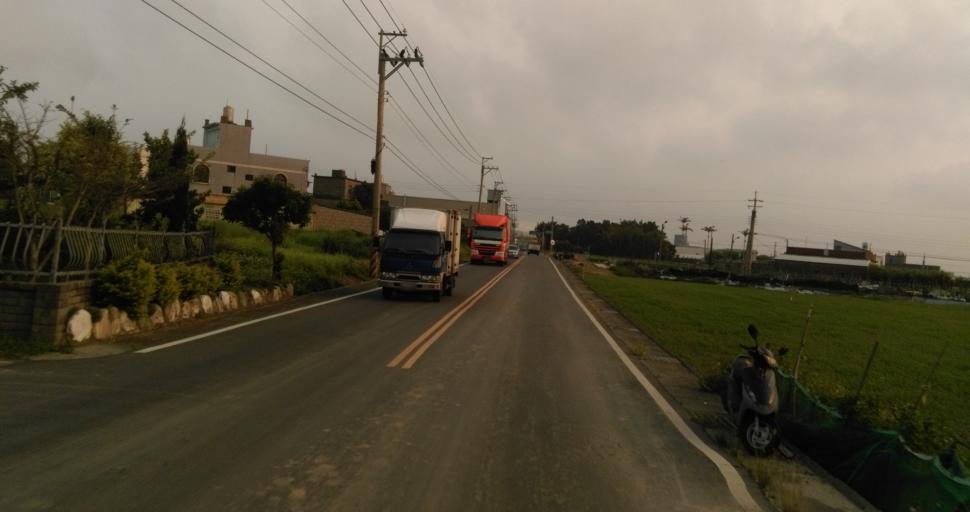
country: TW
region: Taiwan
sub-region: Hsinchu
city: Zhubei
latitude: 24.8647
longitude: 120.9600
